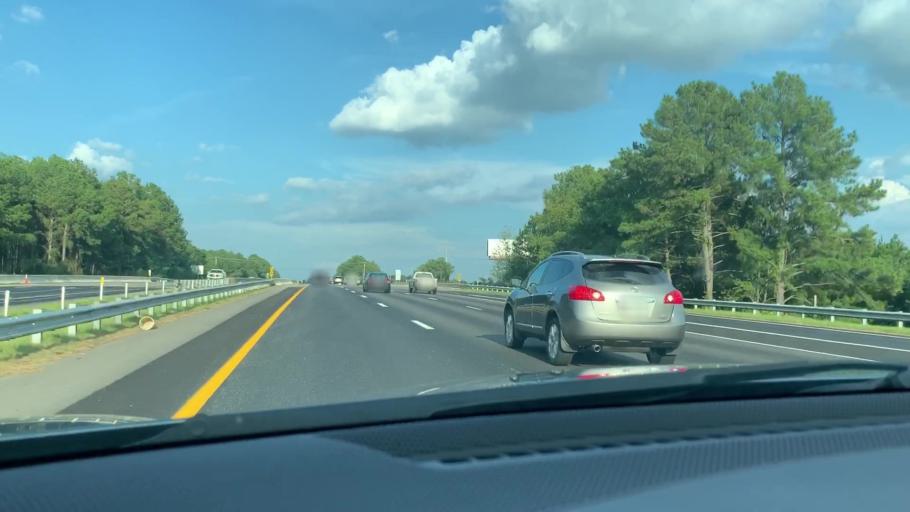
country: US
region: South Carolina
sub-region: Richland County
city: Forest Acres
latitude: 33.9525
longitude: -80.9654
